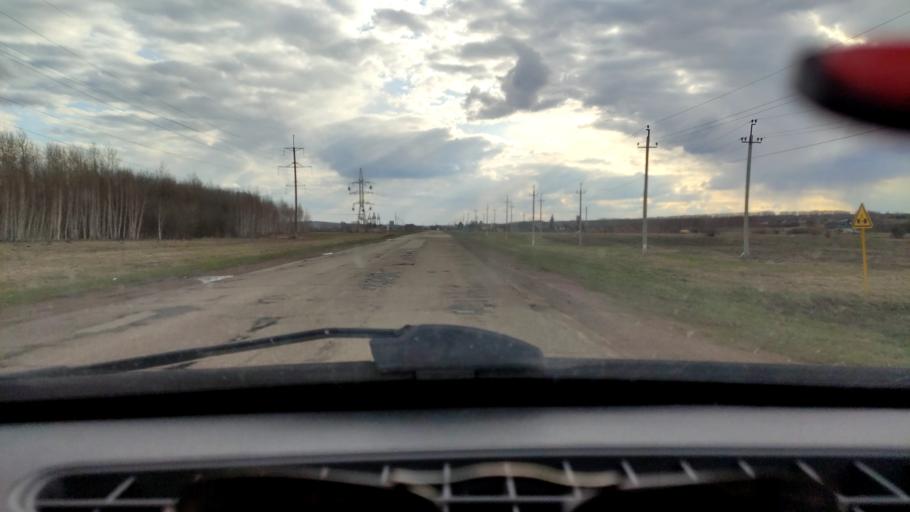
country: RU
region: Bashkortostan
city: Ulukulevo
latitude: 54.4085
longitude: 56.2612
